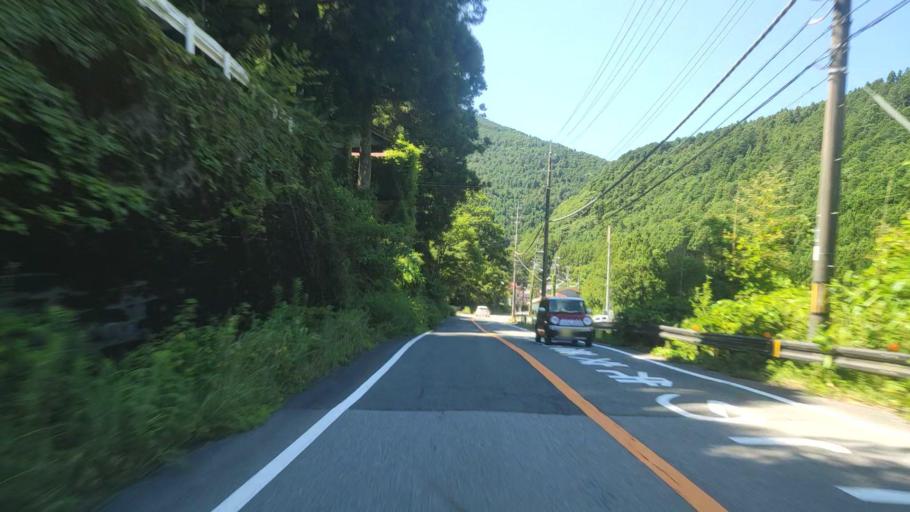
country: JP
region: Nara
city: Yoshino-cho
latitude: 34.2863
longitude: 136.0034
